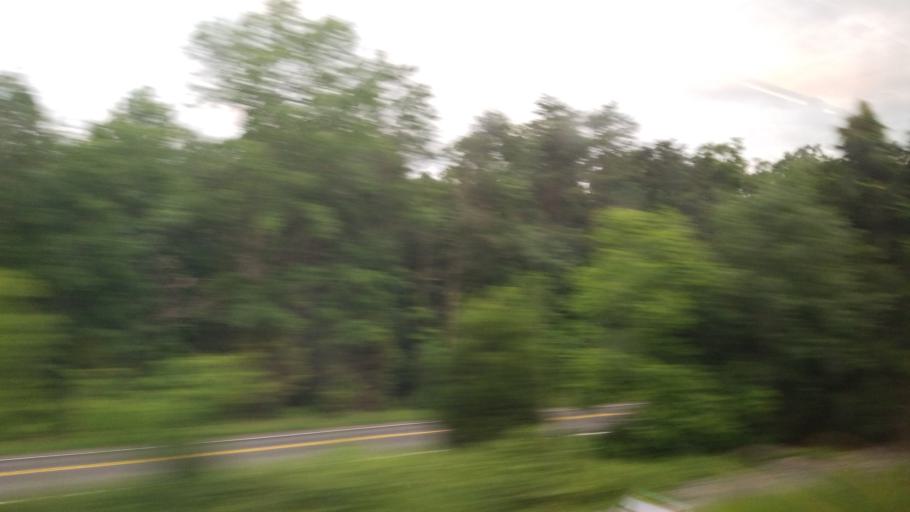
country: US
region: Virginia
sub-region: Culpeper County
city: Culpeper
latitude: 38.4120
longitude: -78.0084
